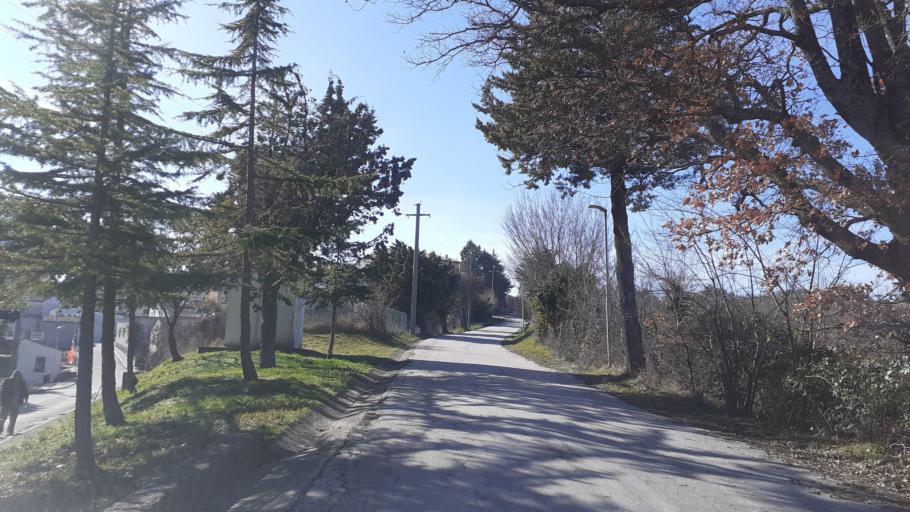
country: IT
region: Molise
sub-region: Provincia di Campobasso
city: Pietracupa
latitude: 41.6840
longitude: 14.5213
